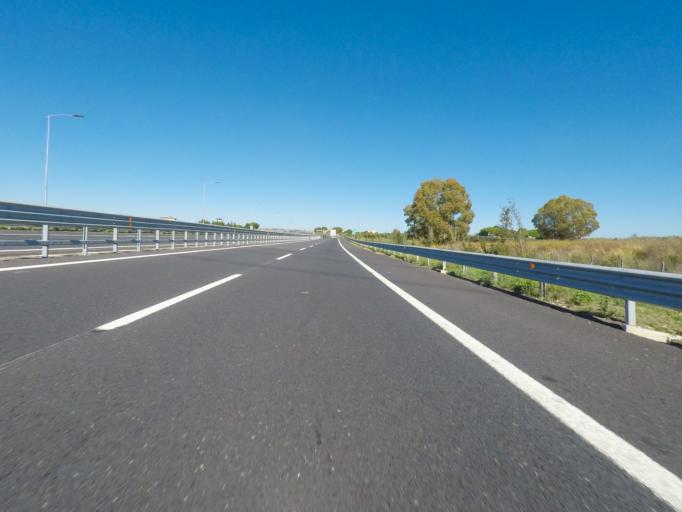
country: IT
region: Latium
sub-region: Citta metropolitana di Roma Capitale
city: Aurelia
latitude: 42.1790
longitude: 11.7884
